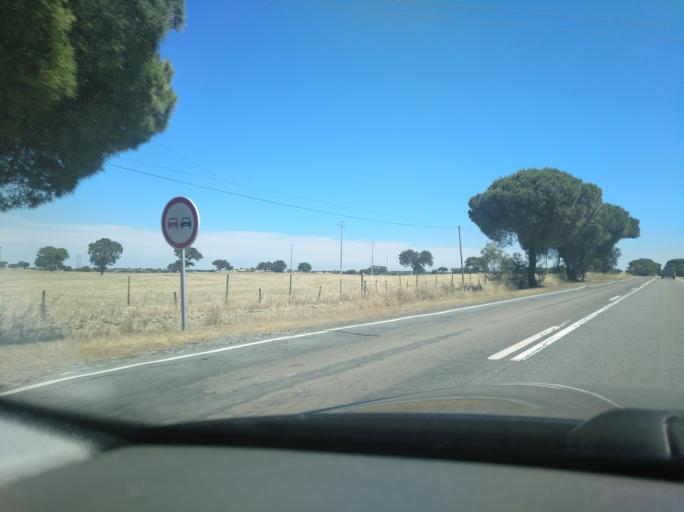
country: PT
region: Beja
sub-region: Almodovar
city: Almodovar
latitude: 37.5734
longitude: -8.0756
